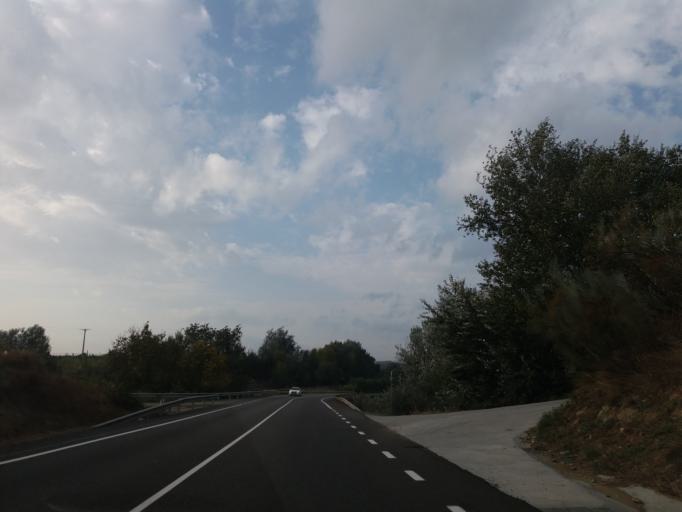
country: ES
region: Catalonia
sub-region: Provincia de Lleida
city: Corbins
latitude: 41.6745
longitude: 0.7137
